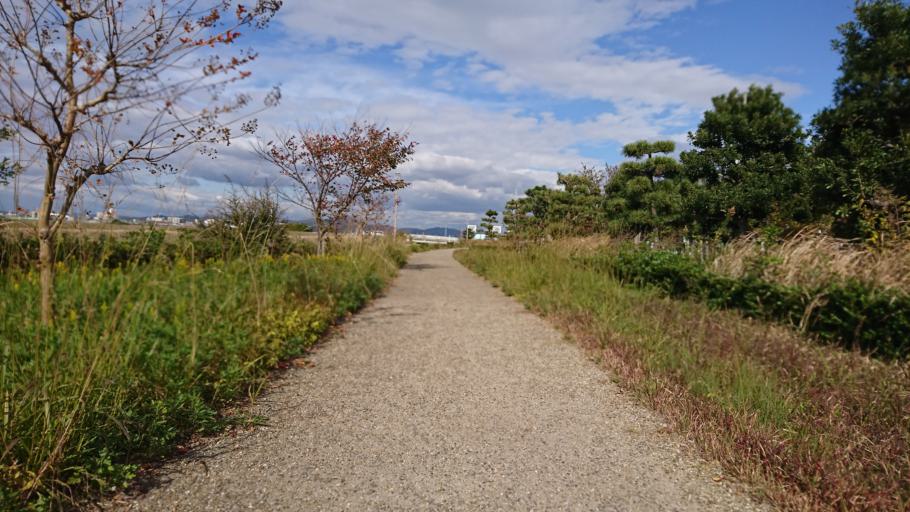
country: JP
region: Hyogo
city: Kakogawacho-honmachi
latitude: 34.7372
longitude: 134.8122
